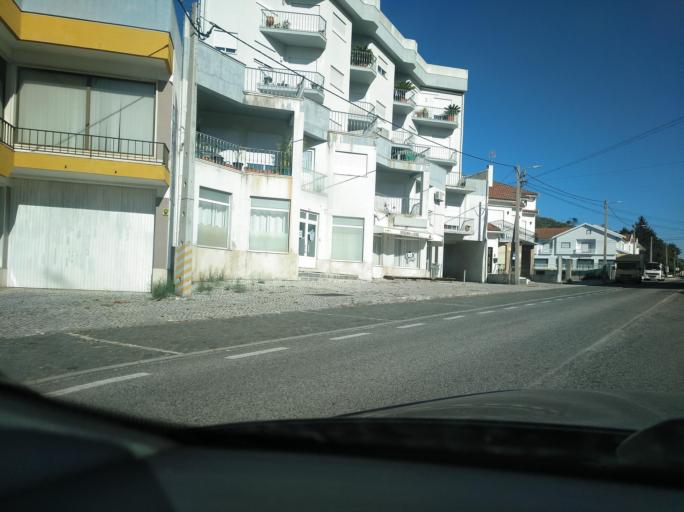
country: PT
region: Santarem
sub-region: Alcanena
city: Alcanena
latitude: 39.5125
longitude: -8.6849
